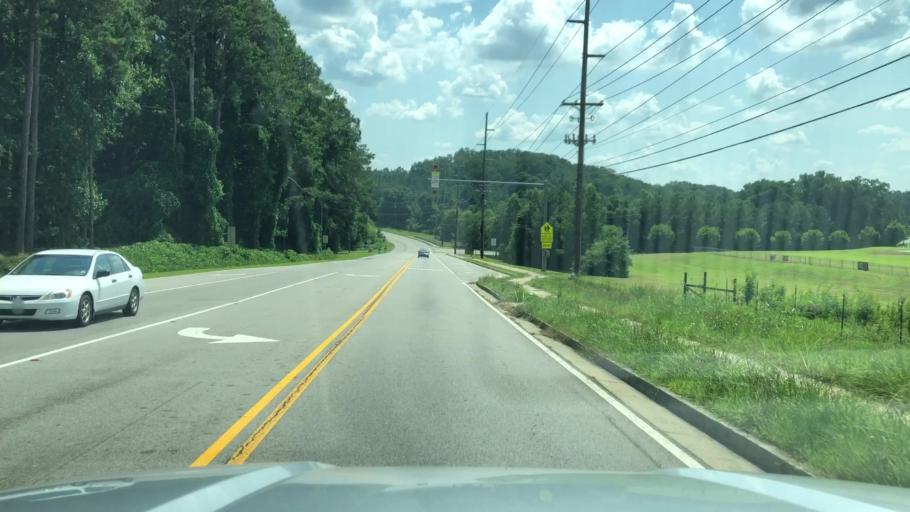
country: US
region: Georgia
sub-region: Cobb County
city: Acworth
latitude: 34.0260
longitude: -84.6970
